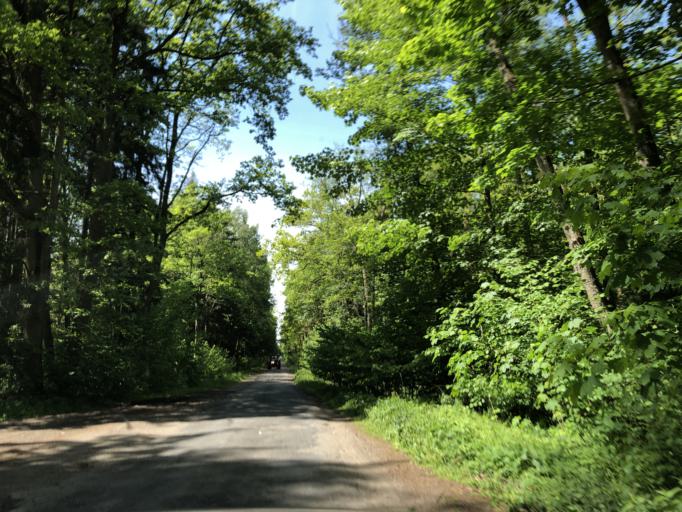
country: PL
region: West Pomeranian Voivodeship
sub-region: Powiat kolobrzeski
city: Dygowo
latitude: 54.0769
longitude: 15.7431
